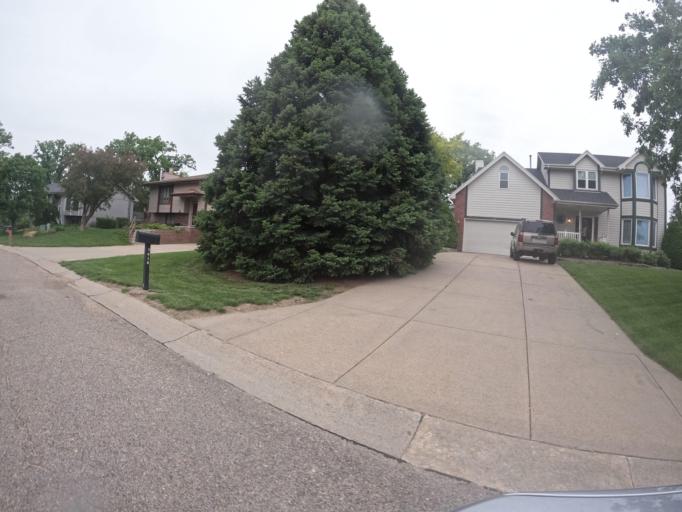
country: US
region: Nebraska
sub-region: Sarpy County
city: Offutt Air Force Base
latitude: 41.0518
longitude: -95.9679
